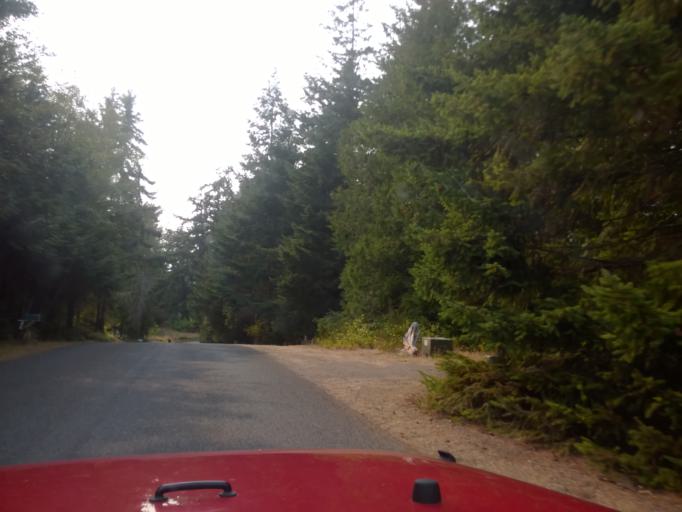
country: US
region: Washington
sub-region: San Juan County
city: Friday Harbor
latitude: 48.5521
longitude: -122.8769
